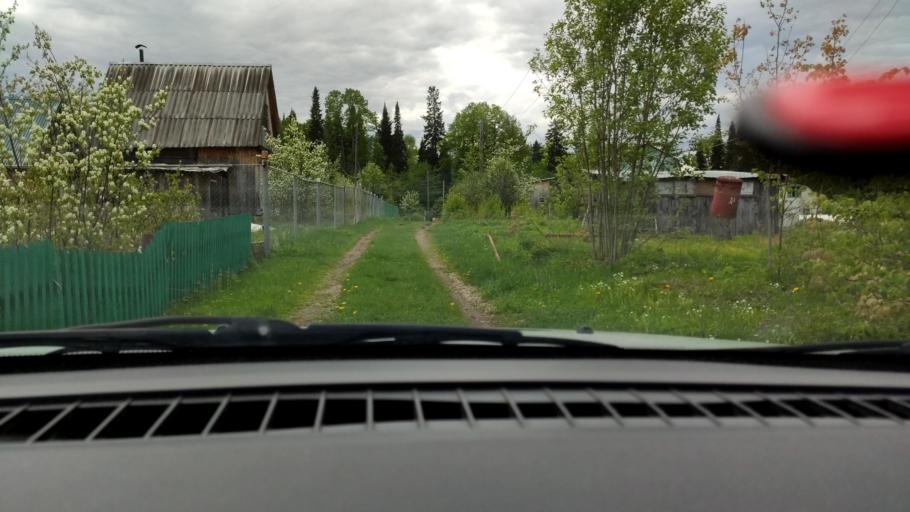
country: RU
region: Perm
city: Bershet'
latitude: 57.7229
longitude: 56.4188
